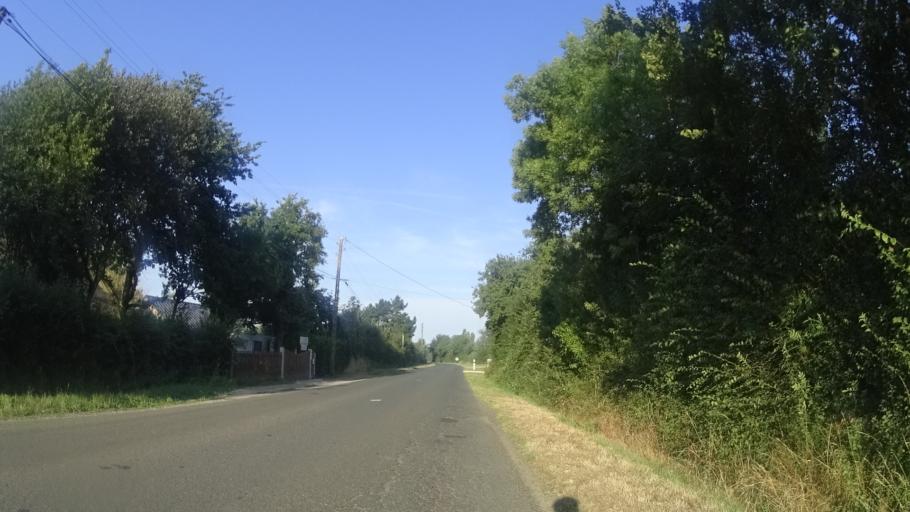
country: FR
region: Pays de la Loire
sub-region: Departement de la Loire-Atlantique
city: Riaille
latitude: 47.4960
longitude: -1.3184
